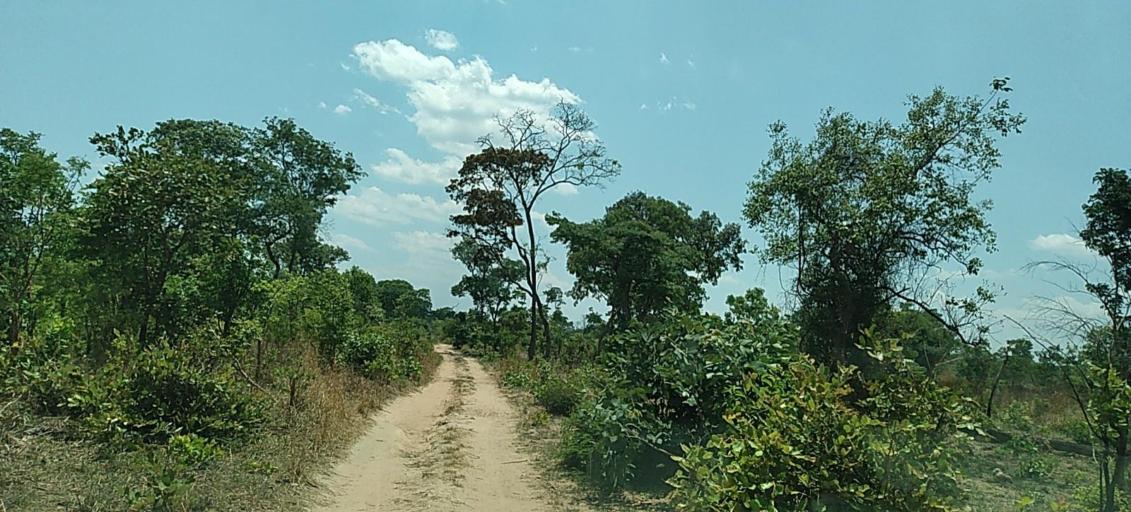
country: ZM
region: Central
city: Kapiri Mposhi
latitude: -13.6327
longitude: 28.7594
